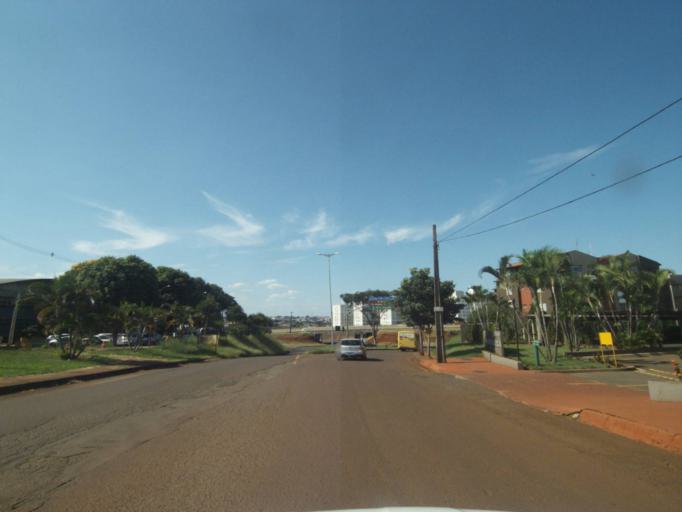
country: BR
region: Parana
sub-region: Londrina
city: Londrina
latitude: -23.3254
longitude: -51.1939
